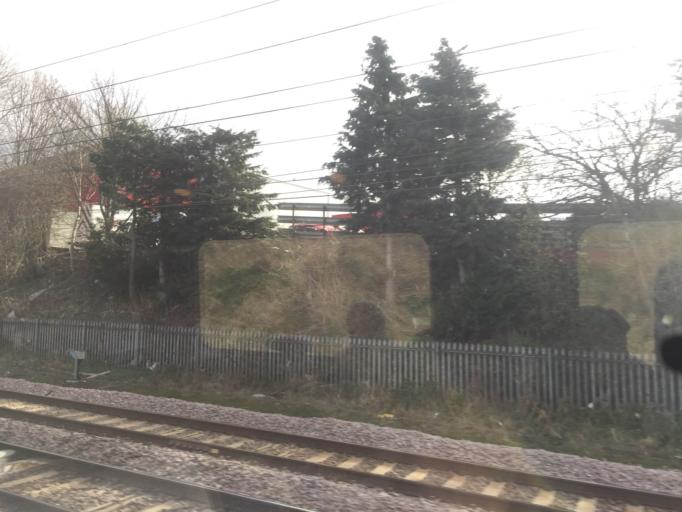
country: GB
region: England
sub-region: Cumbria
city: Penrith
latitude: 54.6574
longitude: -2.7634
